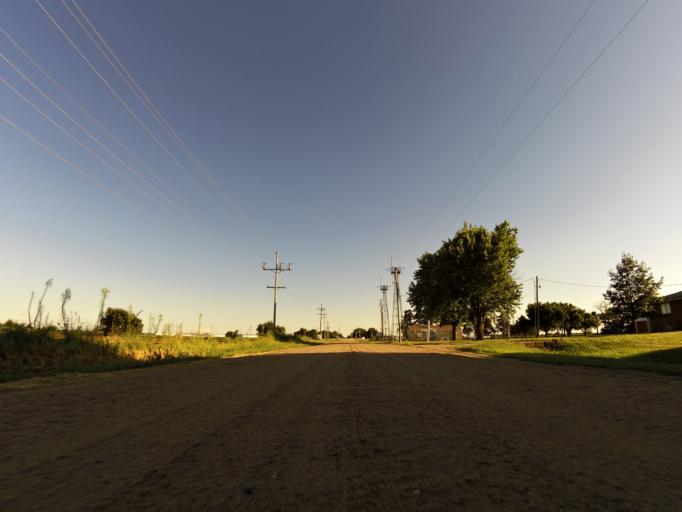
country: US
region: Kansas
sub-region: Reno County
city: South Hutchinson
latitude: 38.0003
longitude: -98.0319
